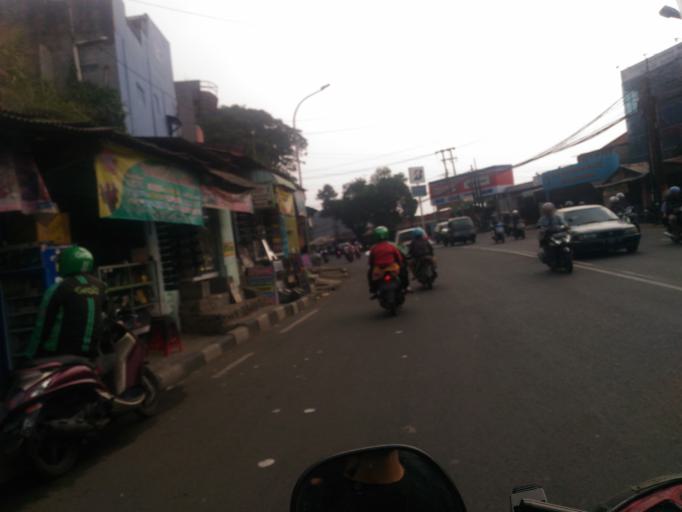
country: ID
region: West Java
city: Bogor
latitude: -6.5613
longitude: 106.8119
